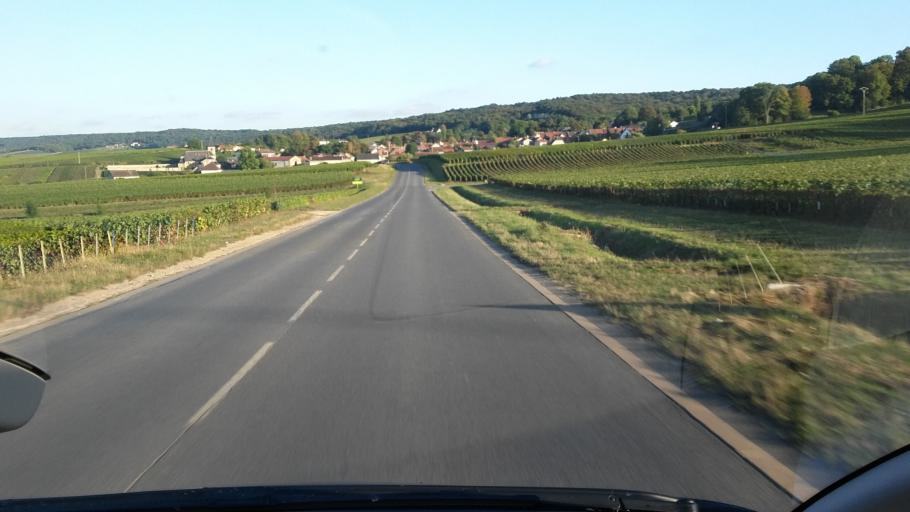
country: FR
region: Champagne-Ardenne
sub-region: Departement de la Marne
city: Rilly-la-Montagne
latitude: 49.1612
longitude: 4.0541
